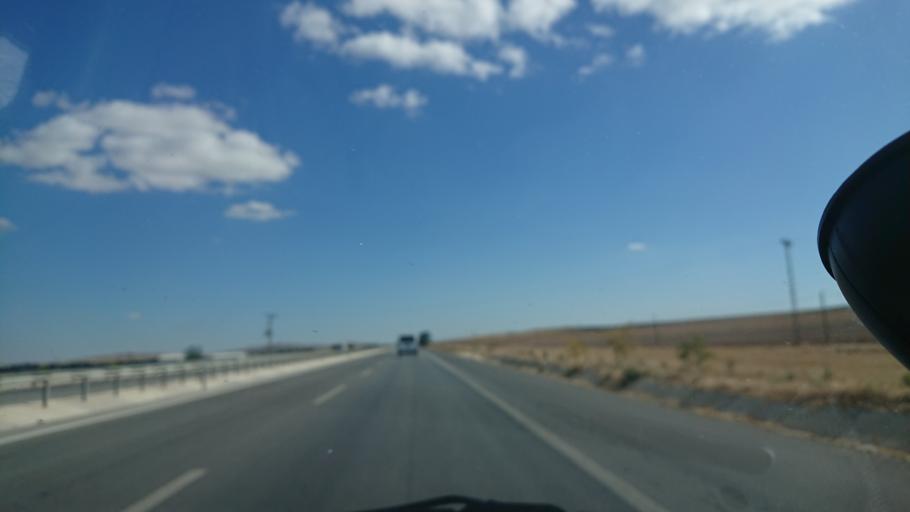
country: TR
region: Eskisehir
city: Mahmudiye
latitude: 39.5300
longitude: 30.9497
